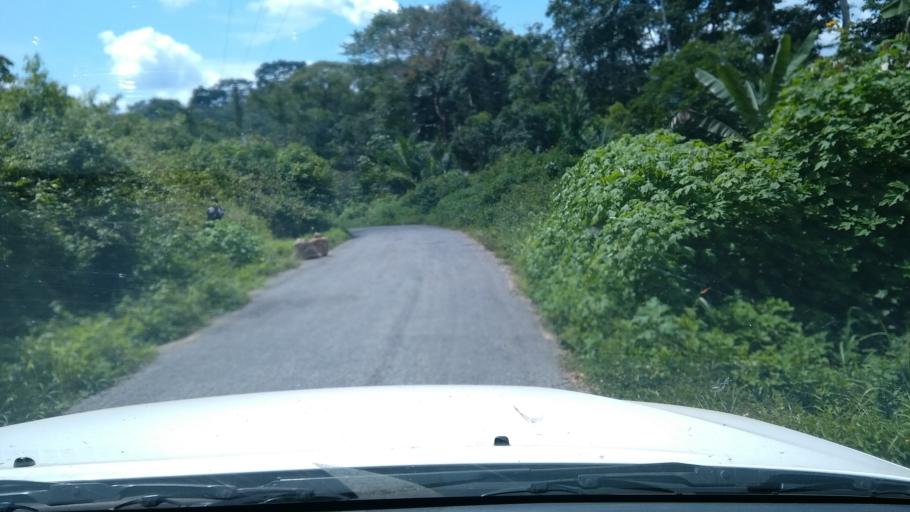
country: CM
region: Centre
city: Evodoula
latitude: 4.1469
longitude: 11.2830
